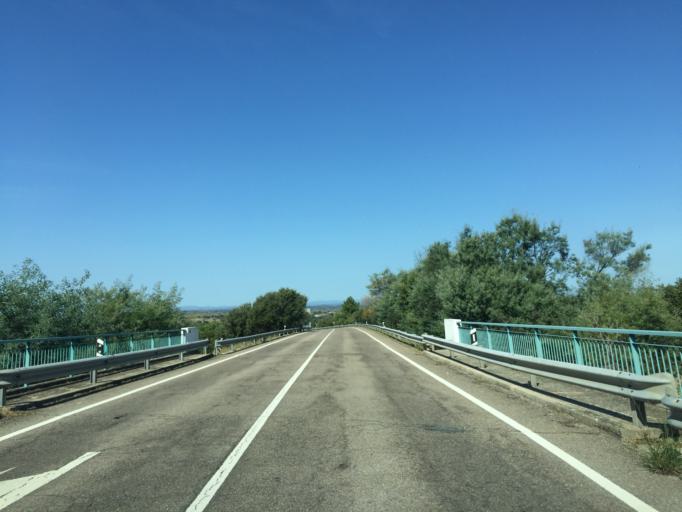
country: PT
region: Portalegre
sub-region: Castelo de Vide
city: Castelo de Vide
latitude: 39.4269
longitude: -7.4835
